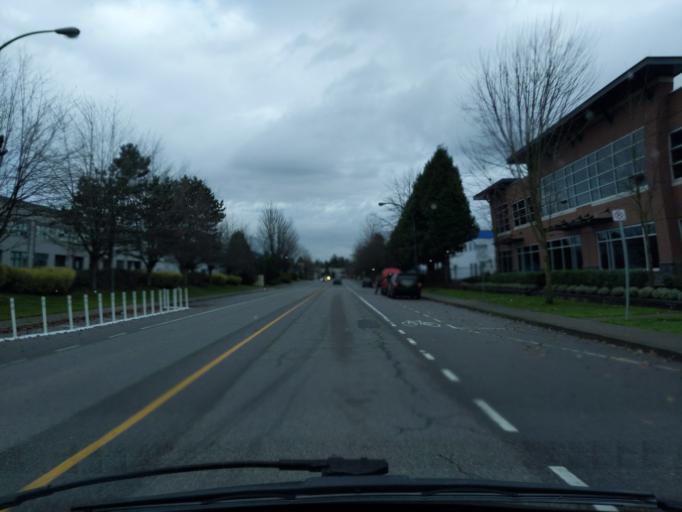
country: CA
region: British Columbia
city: Pitt Meadows
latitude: 49.2093
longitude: -122.6656
